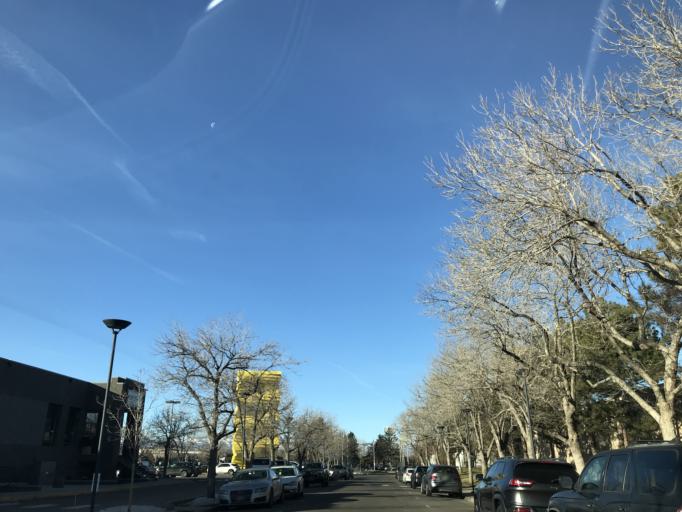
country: US
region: Colorado
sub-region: Denver County
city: Denver
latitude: 39.7058
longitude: -104.9886
